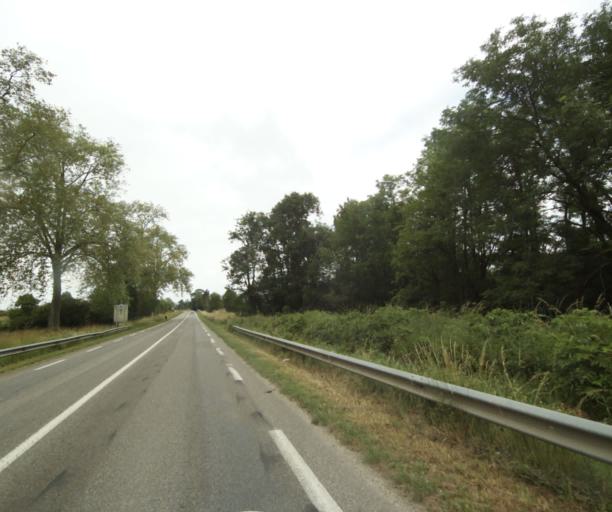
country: FR
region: Midi-Pyrenees
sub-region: Departement du Tarn-et-Garonne
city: Saint-Nauphary
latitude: 43.9707
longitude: 1.4210
